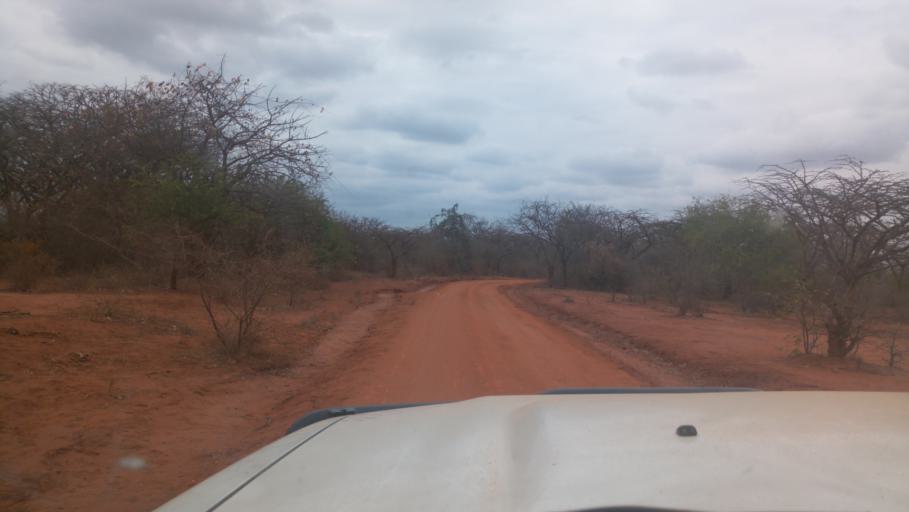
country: KE
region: Makueni
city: Wote
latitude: -1.8466
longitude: 38.0050
